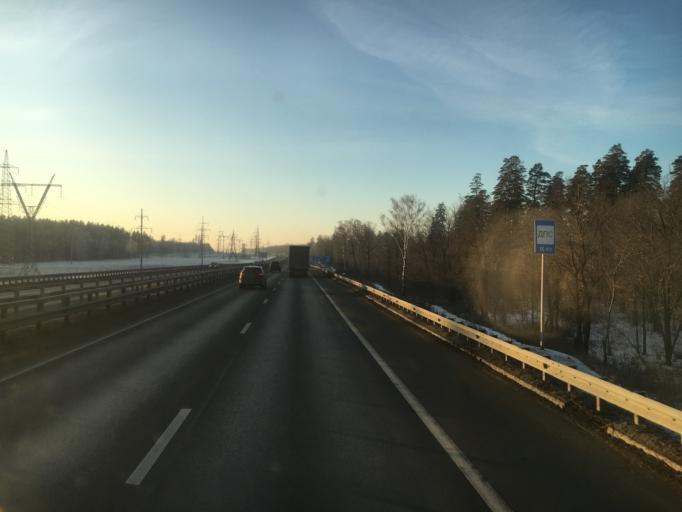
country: RU
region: Samara
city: Pribrezhnyy
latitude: 53.5180
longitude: 49.8312
